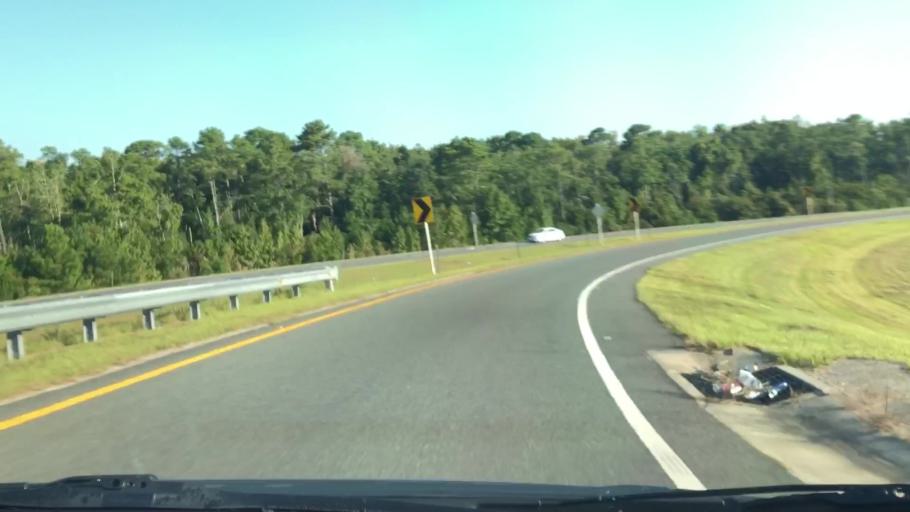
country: US
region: Florida
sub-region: Saint Johns County
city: Palm Valley
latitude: 30.1112
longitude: -81.4497
